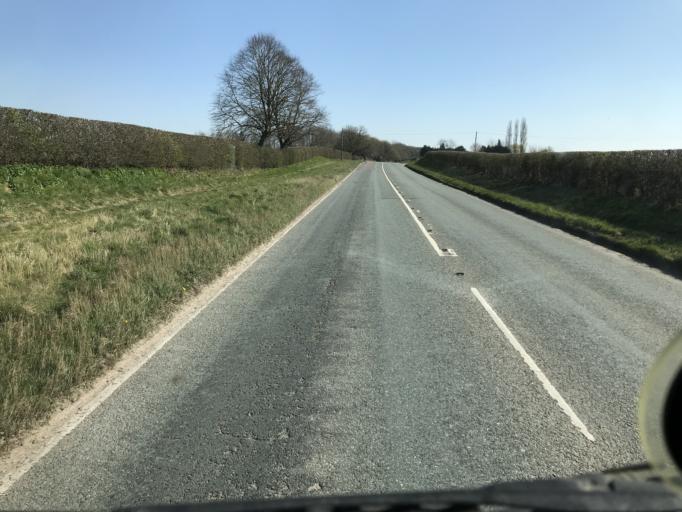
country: GB
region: England
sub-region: Cheshire East
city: Siddington
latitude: 53.2656
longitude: -2.2573
